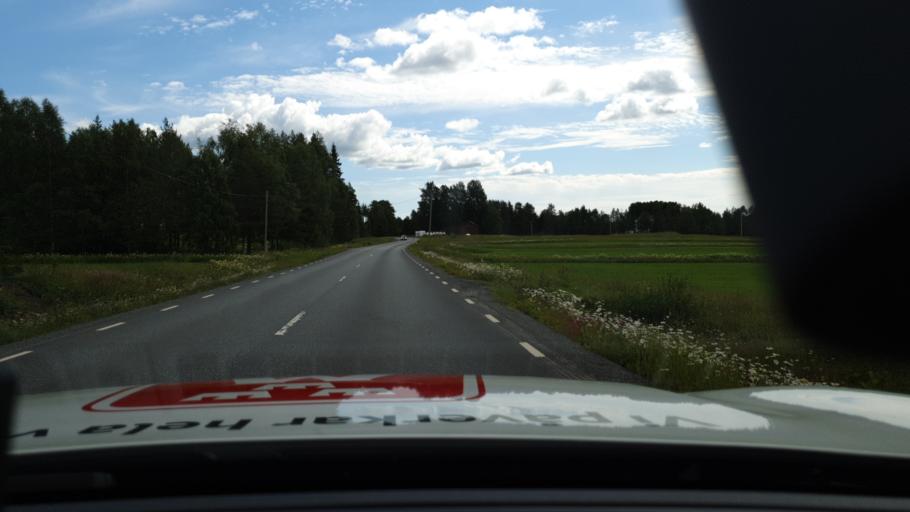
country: SE
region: Norrbotten
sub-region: Lulea Kommun
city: Sodra Sunderbyn
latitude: 65.8260
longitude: 21.9769
